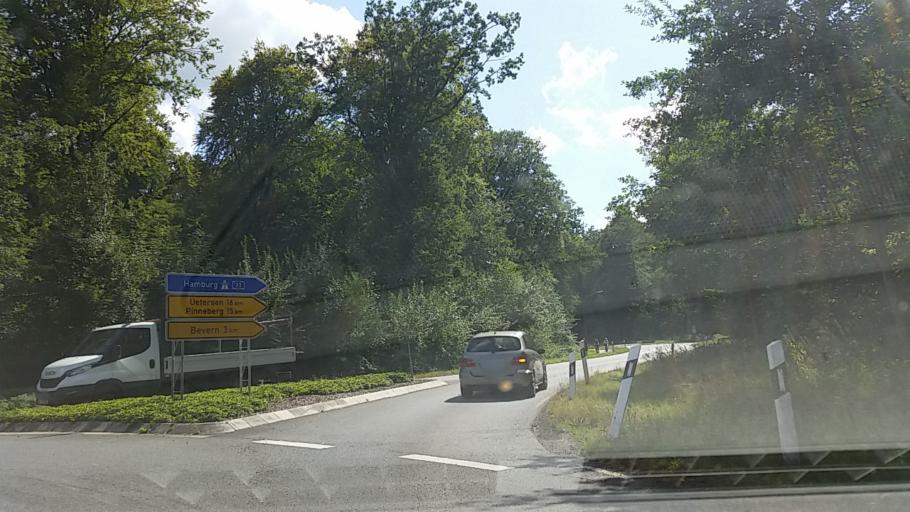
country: DE
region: Schleswig-Holstein
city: Barmstedt
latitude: 53.7816
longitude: 9.7570
